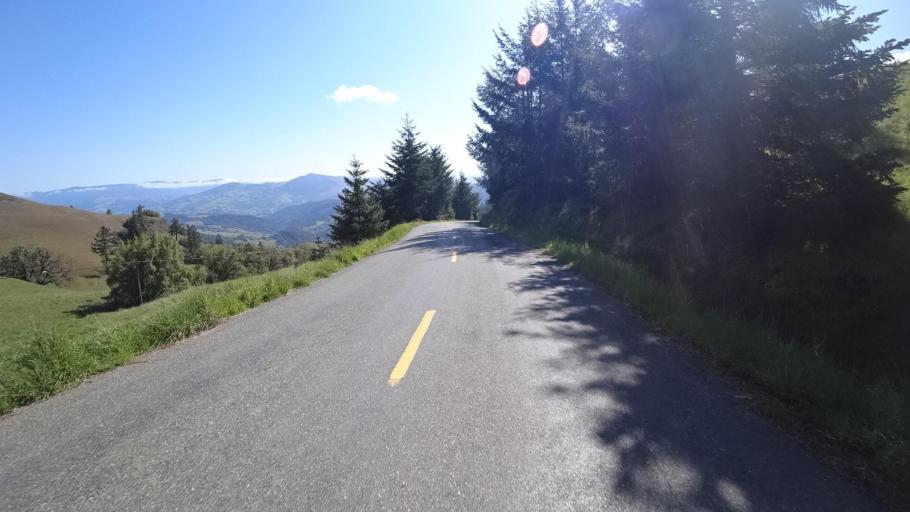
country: US
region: California
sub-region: Humboldt County
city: Redway
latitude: 40.0860
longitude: -123.6715
